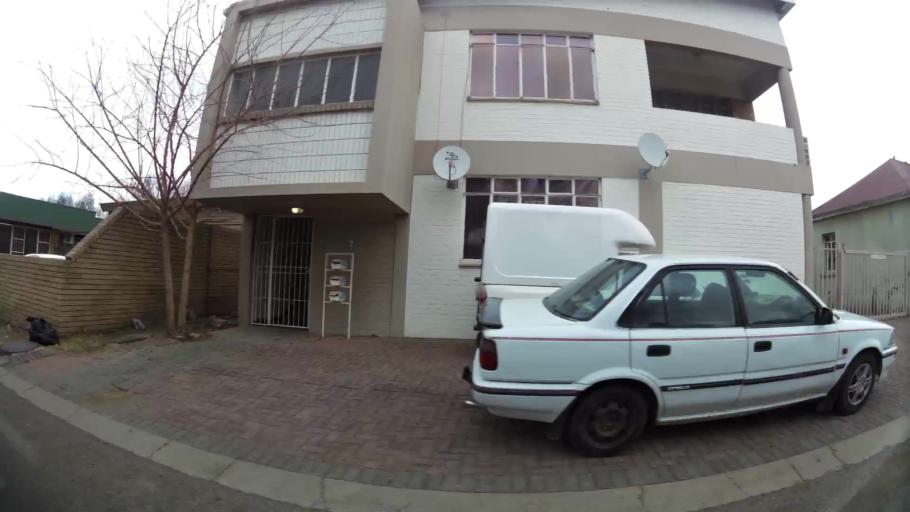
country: ZA
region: Orange Free State
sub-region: Fezile Dabi District Municipality
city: Kroonstad
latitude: -27.6662
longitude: 27.2371
